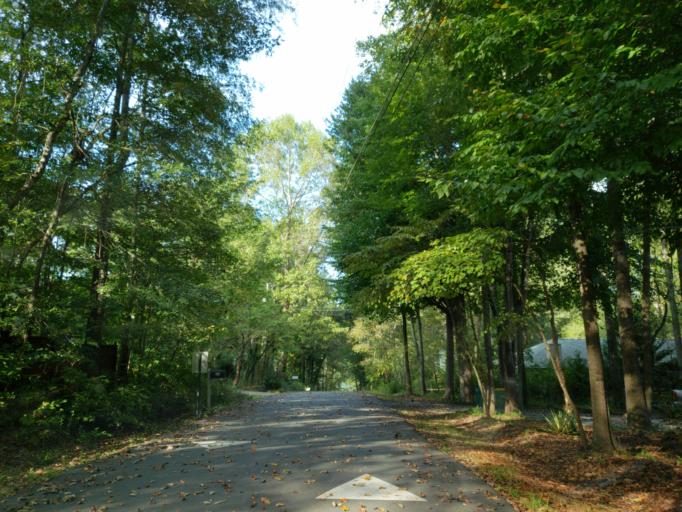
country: US
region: Georgia
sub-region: Fulton County
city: Roswell
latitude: 34.0831
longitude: -84.4173
